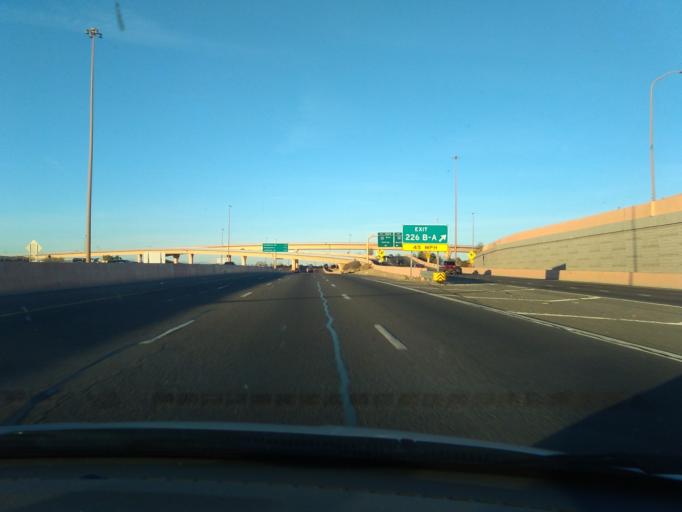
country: US
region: New Mexico
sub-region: Bernalillo County
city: Albuquerque
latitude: 35.1002
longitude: -106.6312
